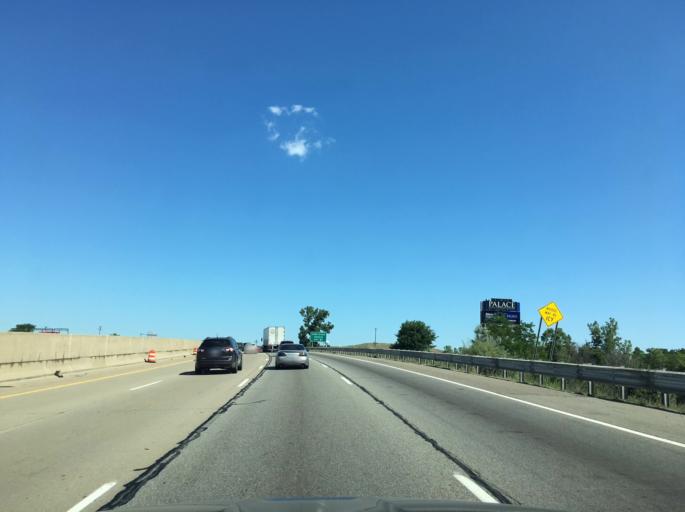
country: US
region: Michigan
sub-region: Oakland County
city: Auburn Hills
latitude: 42.6814
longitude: -83.2417
